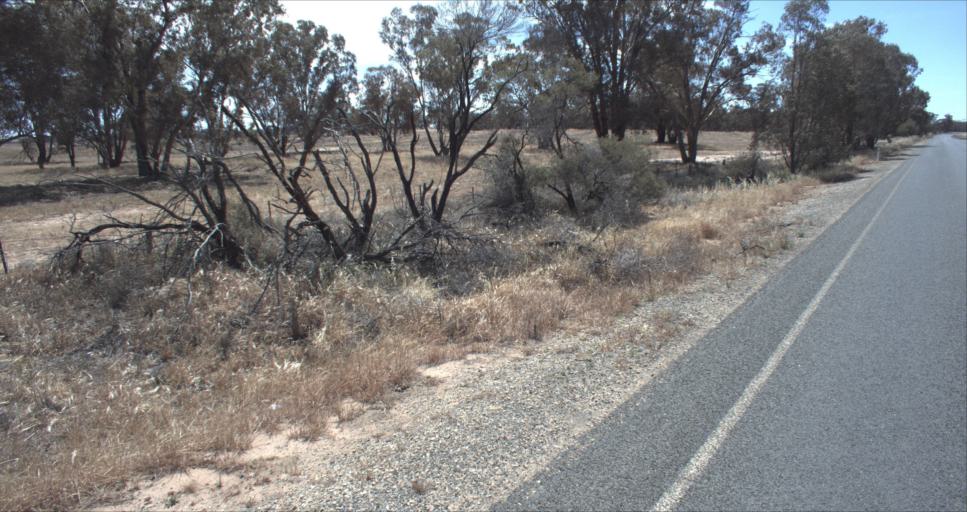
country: AU
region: New South Wales
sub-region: Leeton
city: Leeton
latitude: -34.6573
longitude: 146.4582
